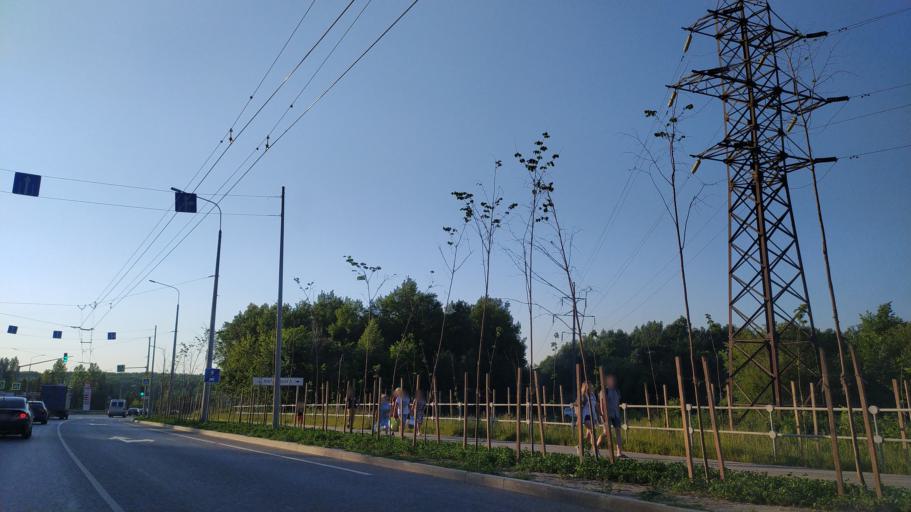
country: RU
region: Chuvashia
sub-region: Cheboksarskiy Rayon
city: Cheboksary
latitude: 56.0807
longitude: 47.2690
